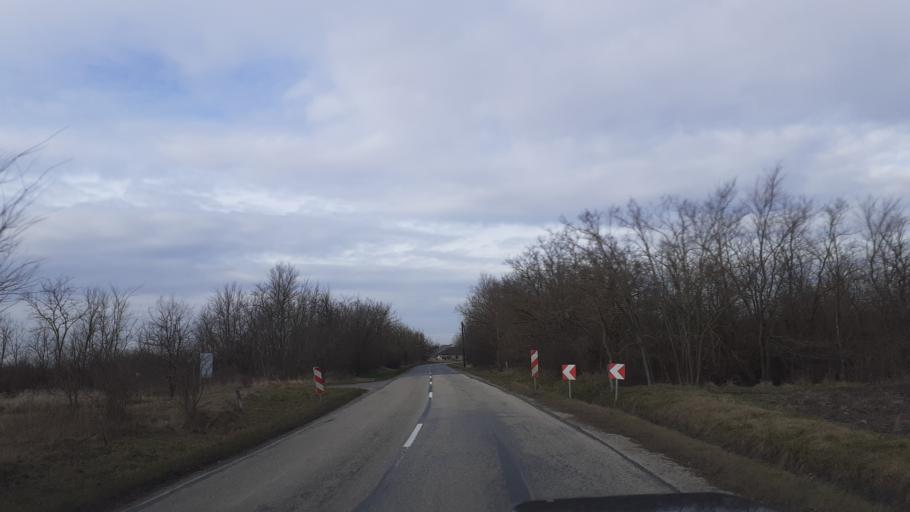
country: HU
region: Fejer
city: Szabadbattyan
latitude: 47.0728
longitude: 18.4155
